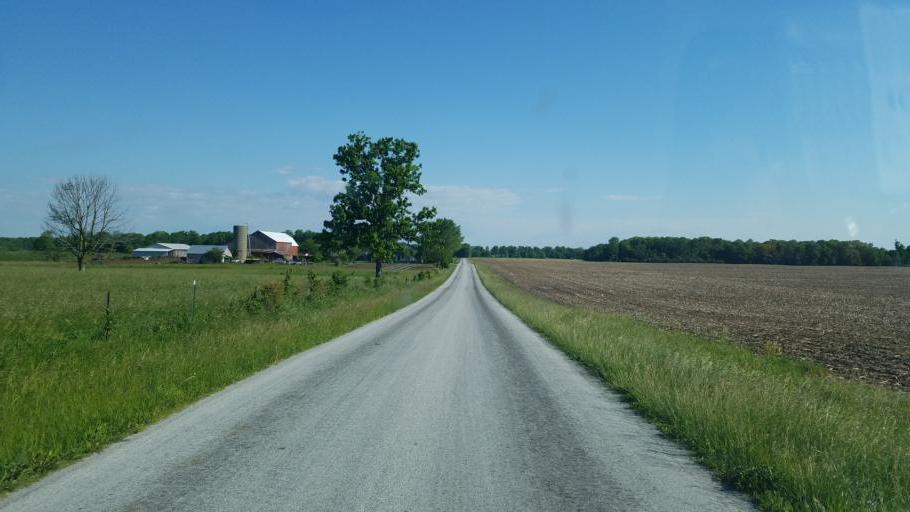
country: US
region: Ohio
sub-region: Hardin County
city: Kenton
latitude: 40.5755
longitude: -83.4697
